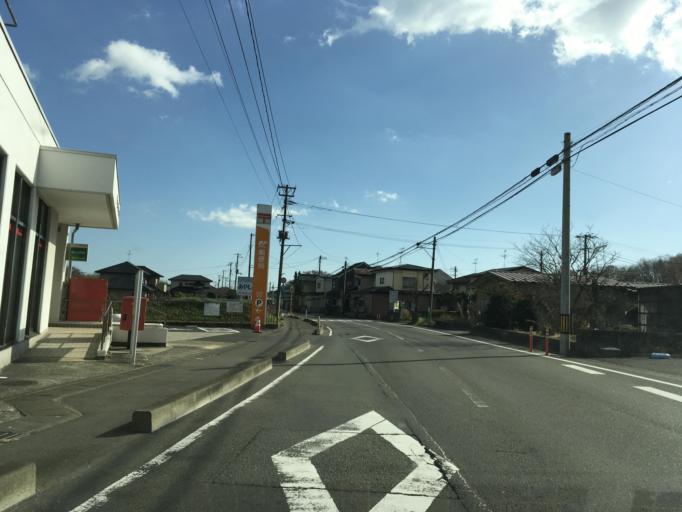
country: JP
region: Miyagi
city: Sendai
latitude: 38.2883
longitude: 140.7485
